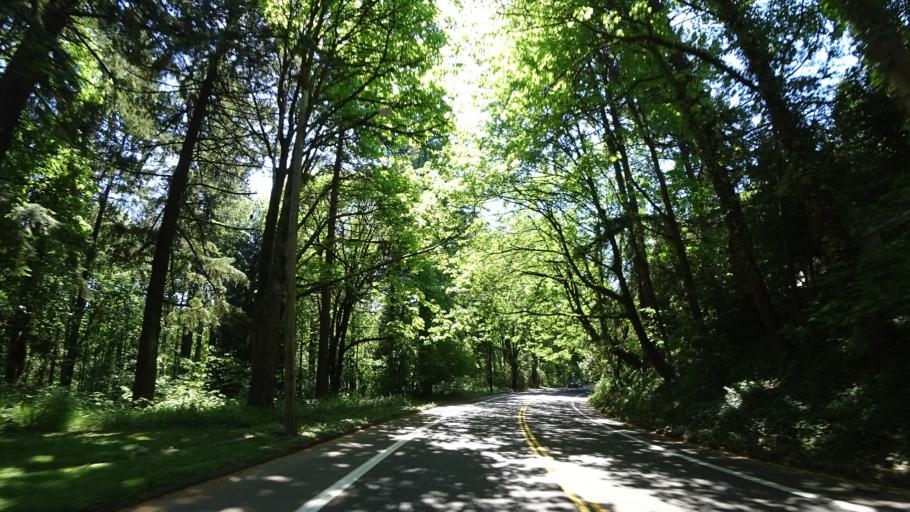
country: US
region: Oregon
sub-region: Multnomah County
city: Portland
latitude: 45.4765
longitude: -122.6843
